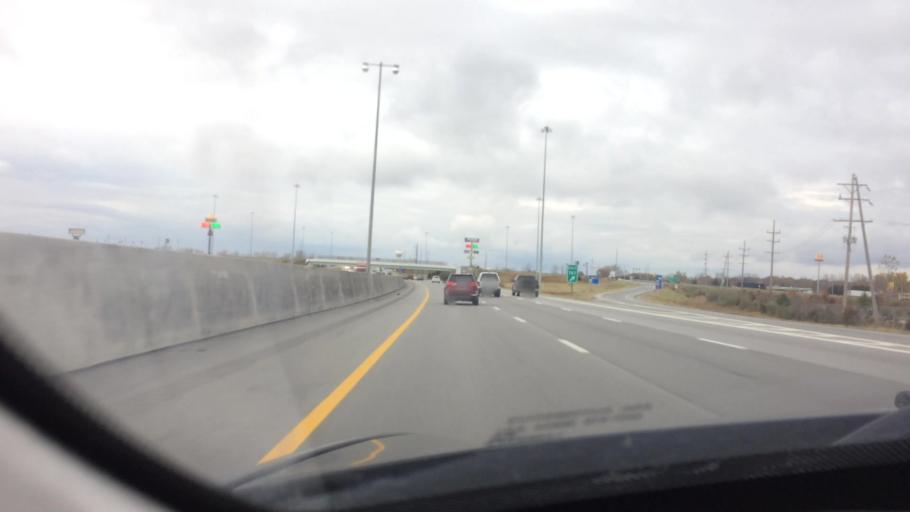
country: US
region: Ohio
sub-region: Wood County
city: North Baltimore
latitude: 41.1688
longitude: -83.6495
